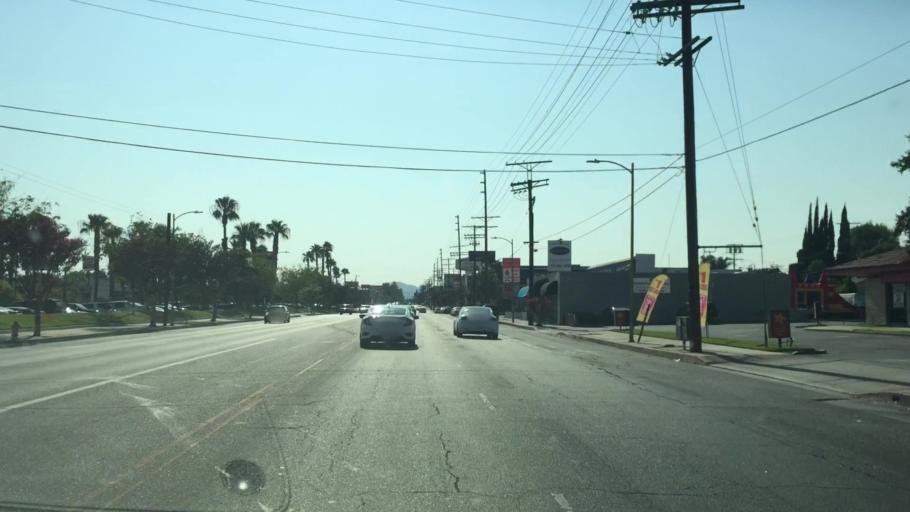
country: US
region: California
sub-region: Los Angeles County
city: Northridge
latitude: 34.2575
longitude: -118.4983
